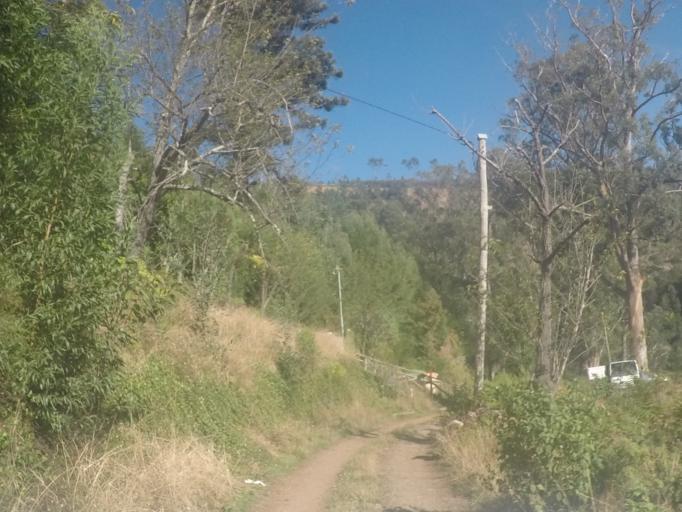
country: PT
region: Madeira
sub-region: Funchal
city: Nossa Senhora do Monte
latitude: 32.6954
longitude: -16.9098
